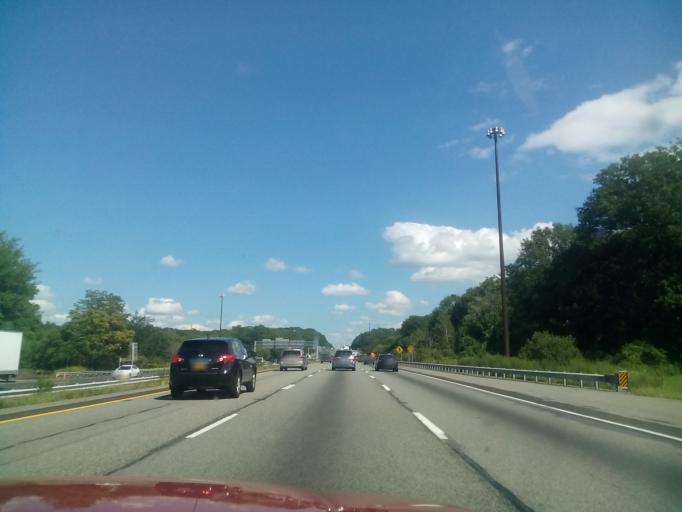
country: US
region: New Jersey
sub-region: Morris County
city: Netcong
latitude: 40.8905
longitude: -74.7018
